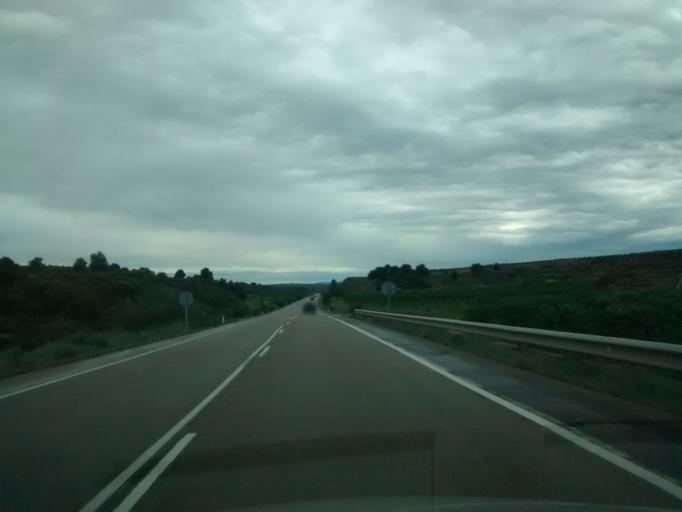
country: ES
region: Aragon
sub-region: Provincia de Zaragoza
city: Maella
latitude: 41.1729
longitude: 0.0671
